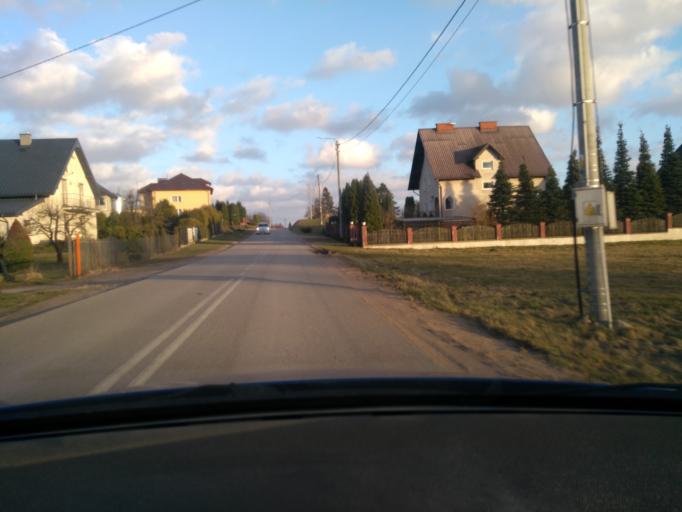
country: PL
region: Pomeranian Voivodeship
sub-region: Powiat kartuski
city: Przodkowo
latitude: 54.4154
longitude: 18.3090
